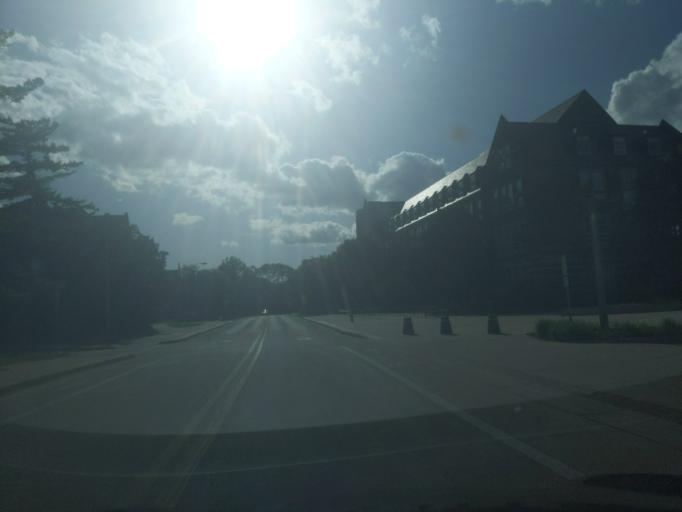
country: US
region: Michigan
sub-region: Ingham County
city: East Lansing
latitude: 42.7325
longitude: -84.4769
